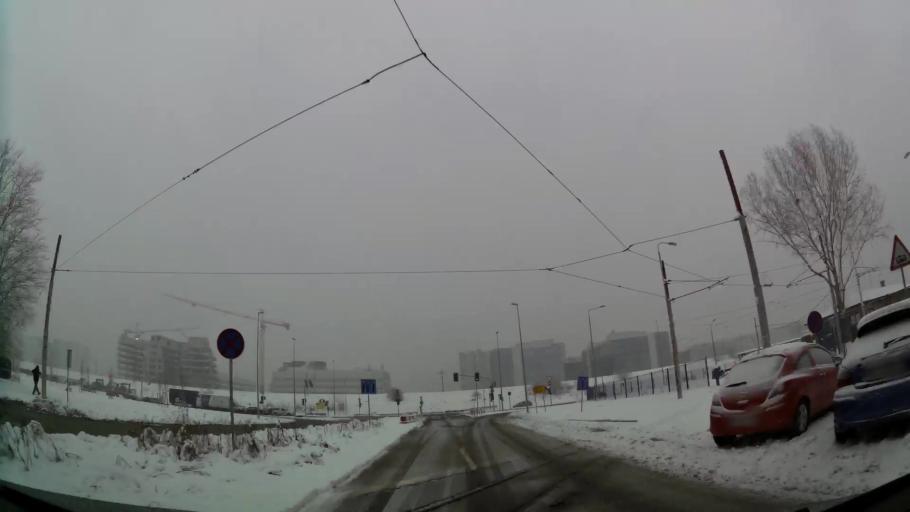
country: RS
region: Central Serbia
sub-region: Belgrade
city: Novi Beograd
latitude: 44.8104
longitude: 20.4067
